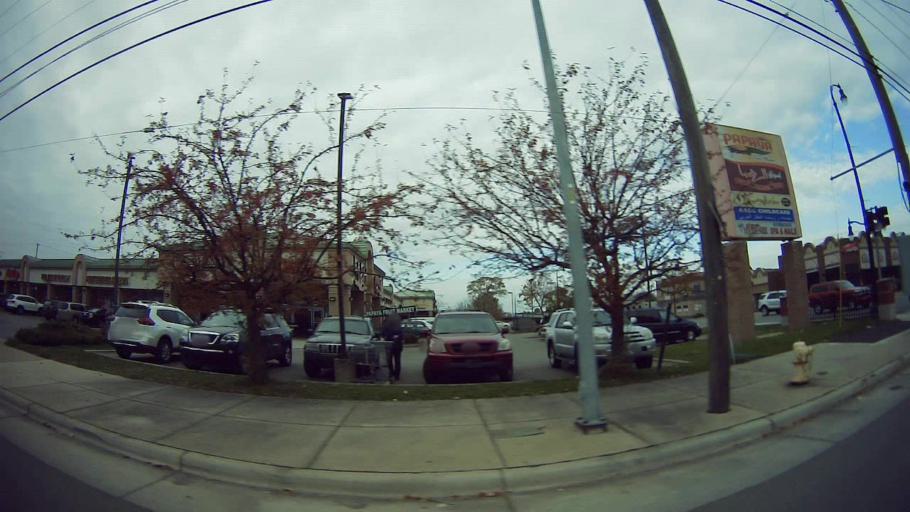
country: US
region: Michigan
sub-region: Wayne County
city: Dearborn
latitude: 42.3441
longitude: -83.1865
